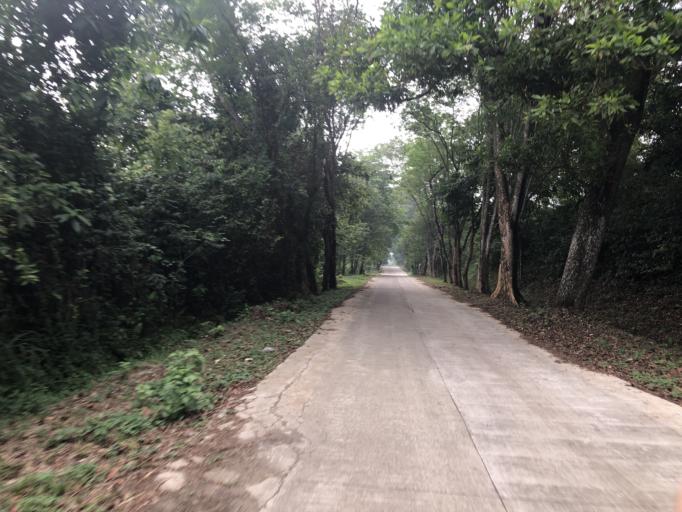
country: ID
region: West Java
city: Ciampea
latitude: -6.5543
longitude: 106.7169
